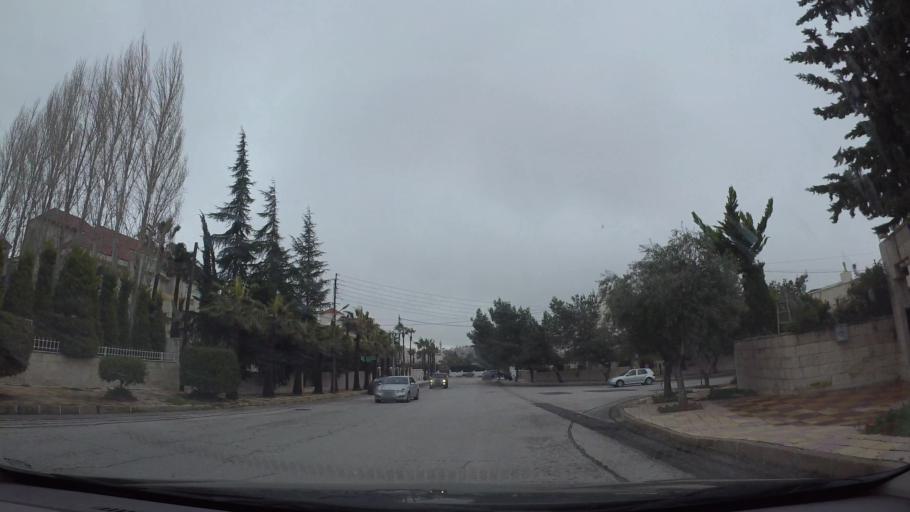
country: JO
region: Amman
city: Al Bunayyat ash Shamaliyah
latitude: 31.9445
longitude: 35.8763
